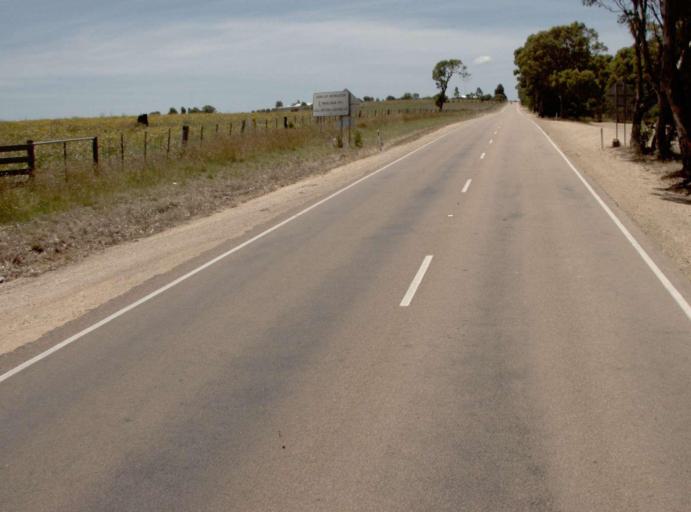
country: AU
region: Victoria
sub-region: East Gippsland
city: Bairnsdale
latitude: -37.8053
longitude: 147.6513
